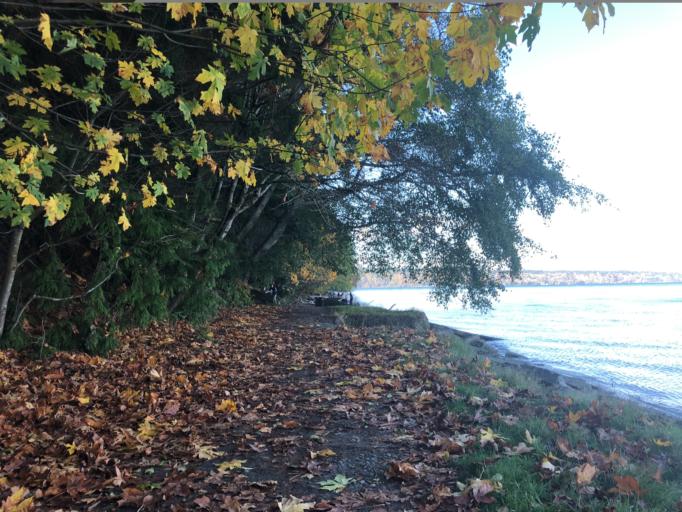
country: US
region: Washington
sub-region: Pierce County
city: Gig Harbor
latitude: 47.3149
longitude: -122.5309
